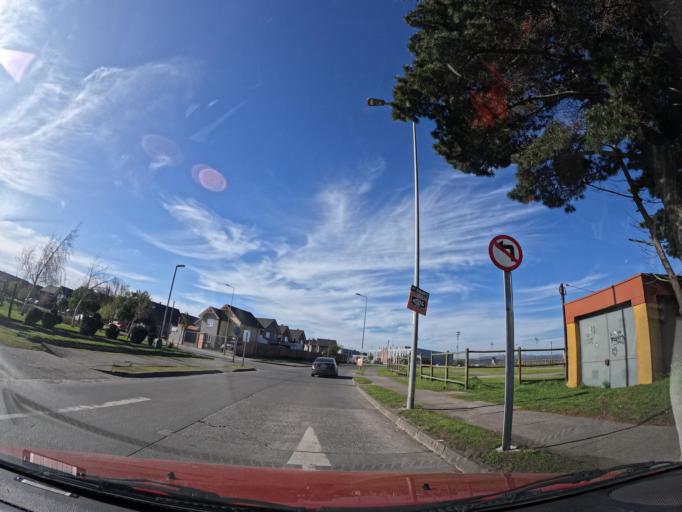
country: CL
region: Biobio
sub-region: Provincia de Concepcion
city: Concepcion
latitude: -36.7739
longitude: -73.0684
